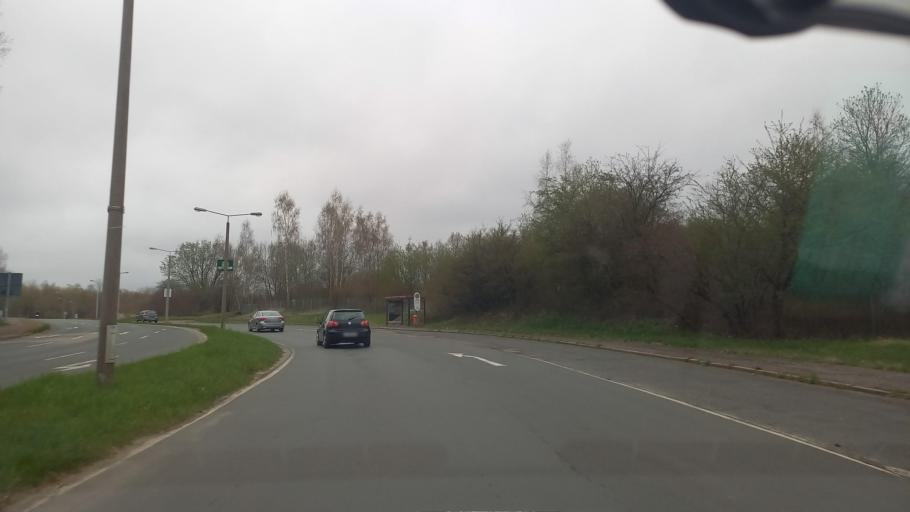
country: DE
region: Saxony
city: Lichtentanne
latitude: 50.7066
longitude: 12.4592
